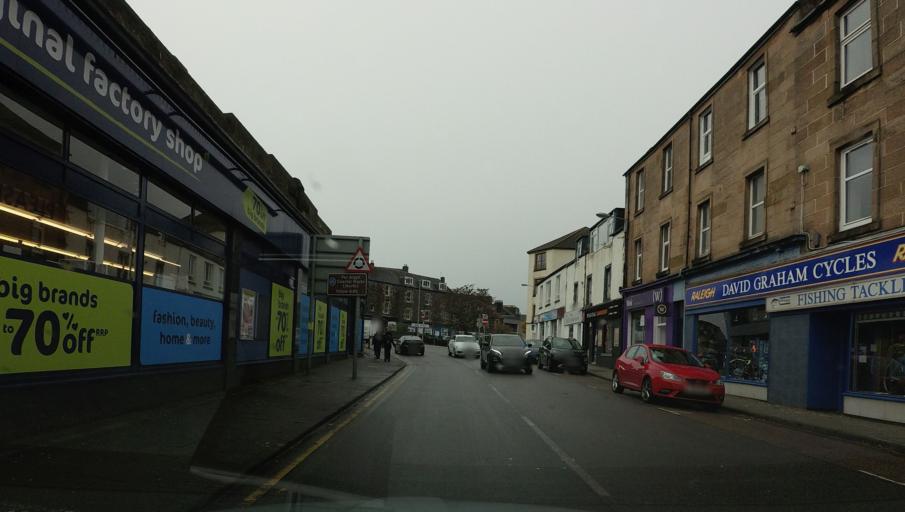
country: GB
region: Scotland
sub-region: Argyll and Bute
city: Oban
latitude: 56.4112
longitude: -5.4704
